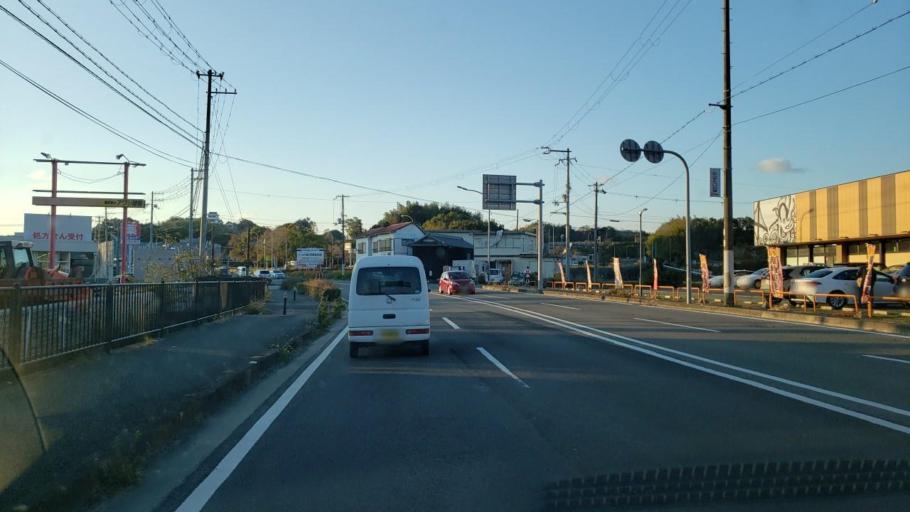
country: JP
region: Hyogo
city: Sumoto
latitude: 34.4393
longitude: 134.8766
